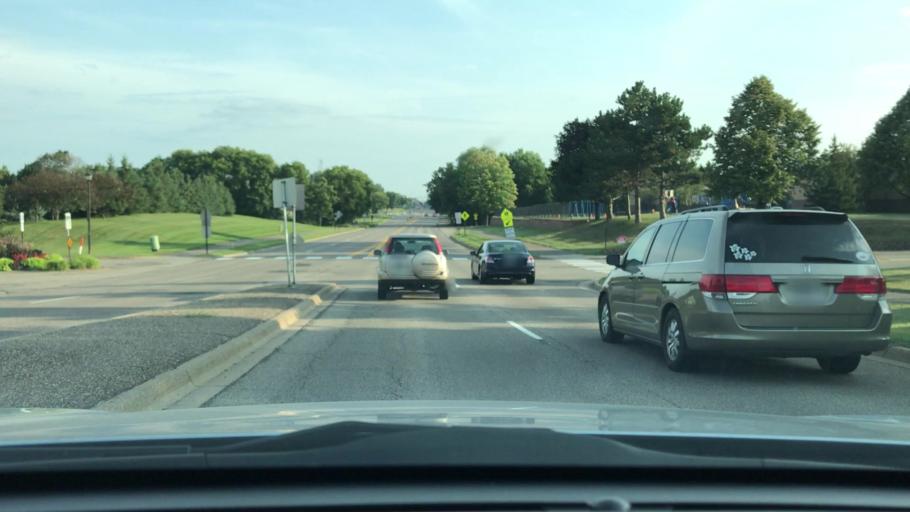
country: US
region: Minnesota
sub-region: Hennepin County
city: Plymouth
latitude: 45.0312
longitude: -93.4818
